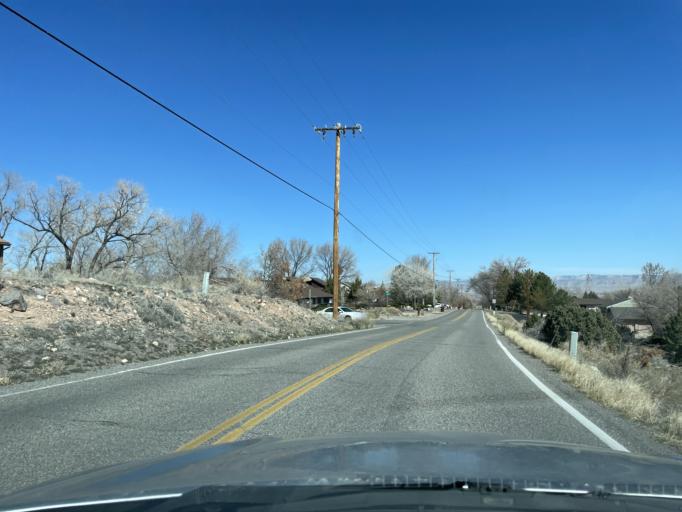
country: US
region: Colorado
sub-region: Mesa County
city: Redlands
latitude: 39.0784
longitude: -108.6688
